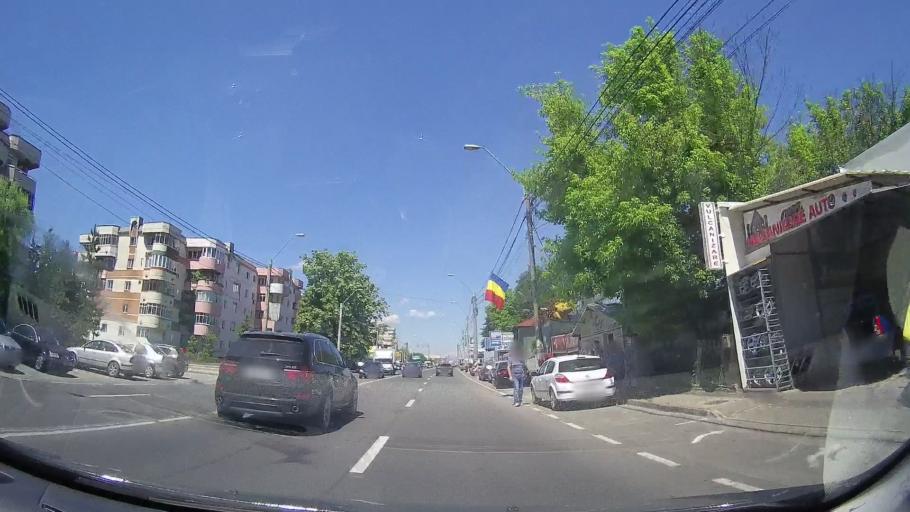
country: RO
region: Arges
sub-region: Comuna Bascov
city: Bascov
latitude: 44.8775
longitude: 24.8431
